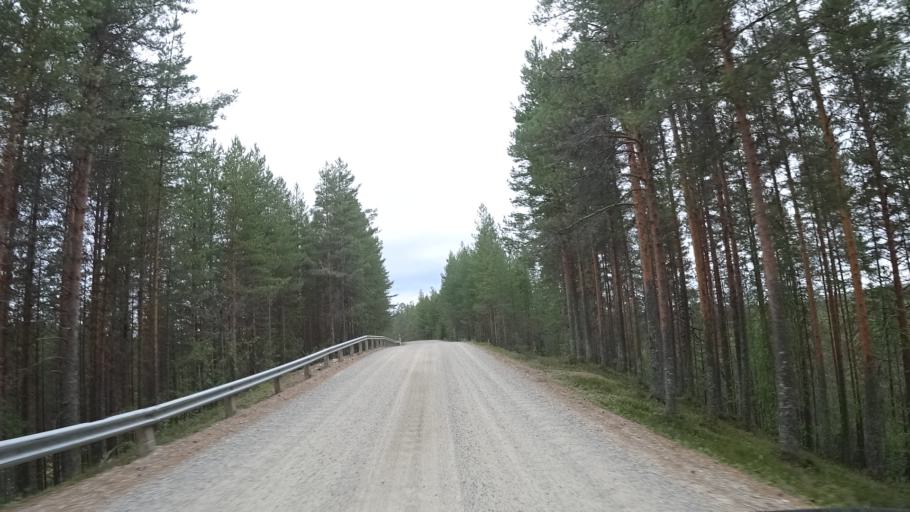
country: FI
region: North Karelia
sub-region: Pielisen Karjala
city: Lieksa
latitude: 63.2348
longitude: 30.3640
